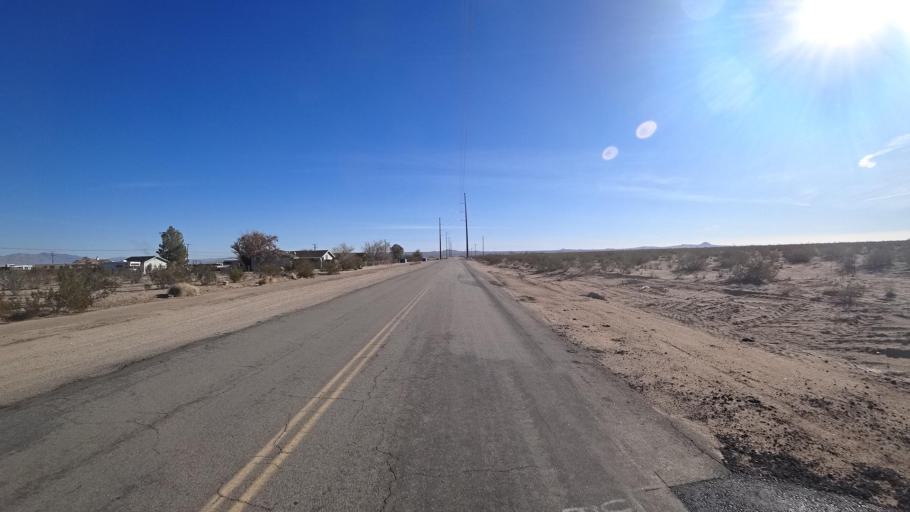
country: US
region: California
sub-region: Kern County
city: California City
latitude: 35.1987
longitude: -118.0150
